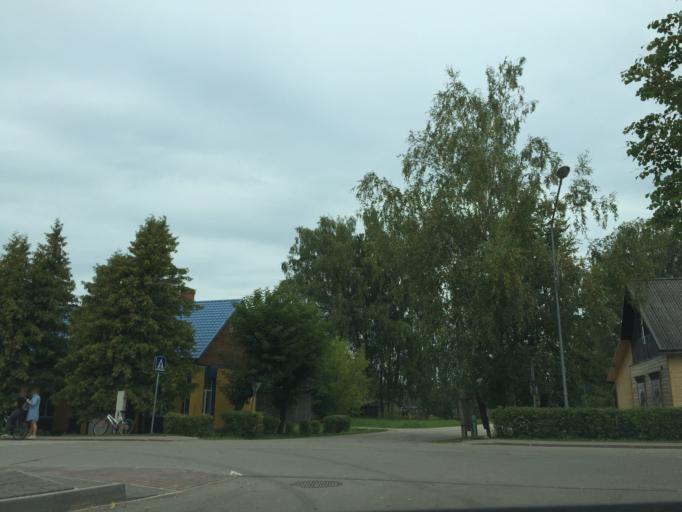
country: LV
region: Zilupes
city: Zilupe
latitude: 56.3889
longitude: 28.1208
